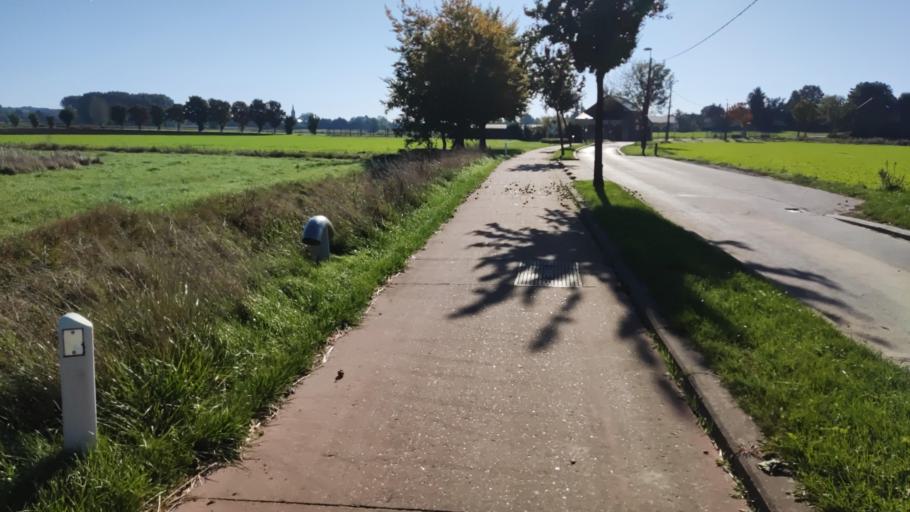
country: BE
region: Flanders
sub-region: Provincie Vlaams-Brabant
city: Tienen
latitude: 50.8193
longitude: 5.0047
